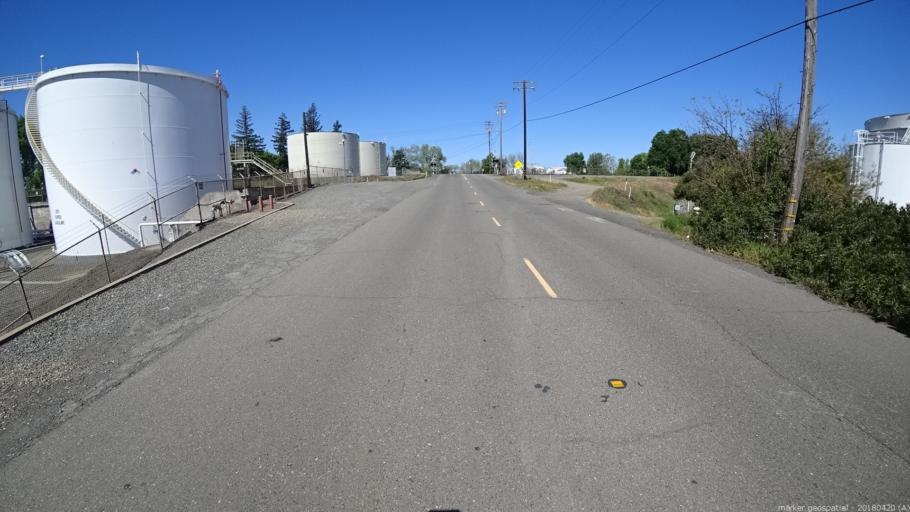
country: US
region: California
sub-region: Yolo County
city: West Sacramento
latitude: 38.5677
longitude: -121.5152
